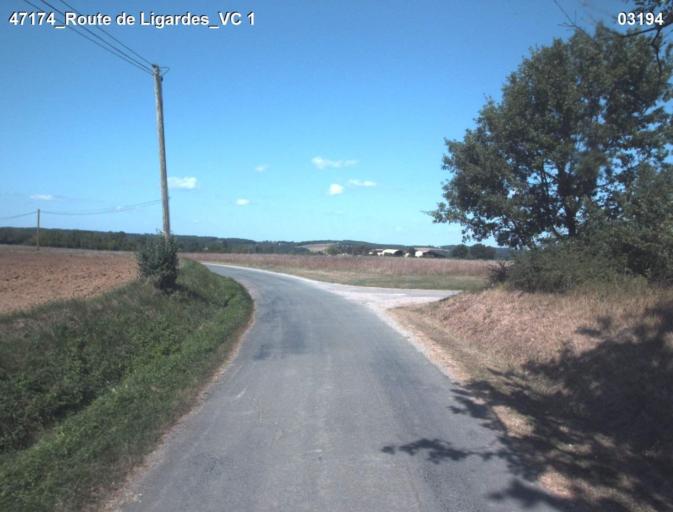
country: FR
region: Midi-Pyrenees
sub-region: Departement du Gers
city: Condom
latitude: 44.0336
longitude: 0.3828
